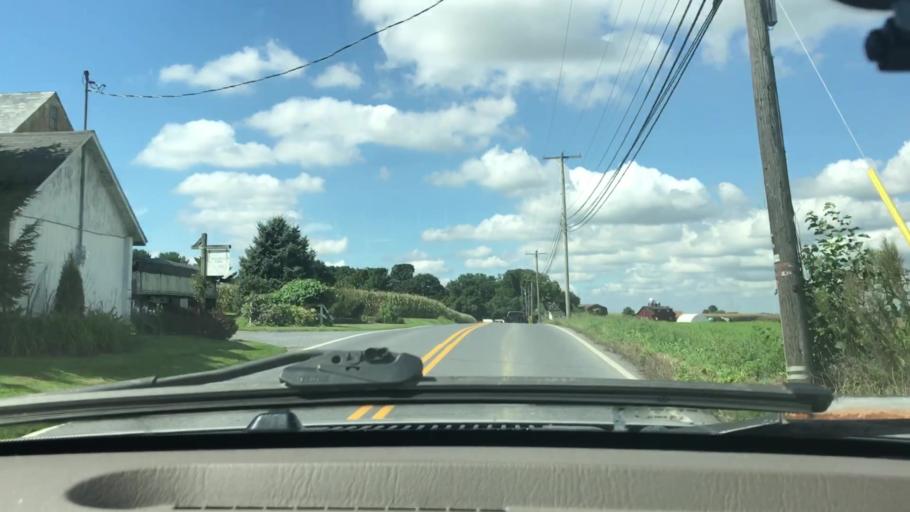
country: US
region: Pennsylvania
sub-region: Lancaster County
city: East Petersburg
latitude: 40.1134
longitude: -76.3799
